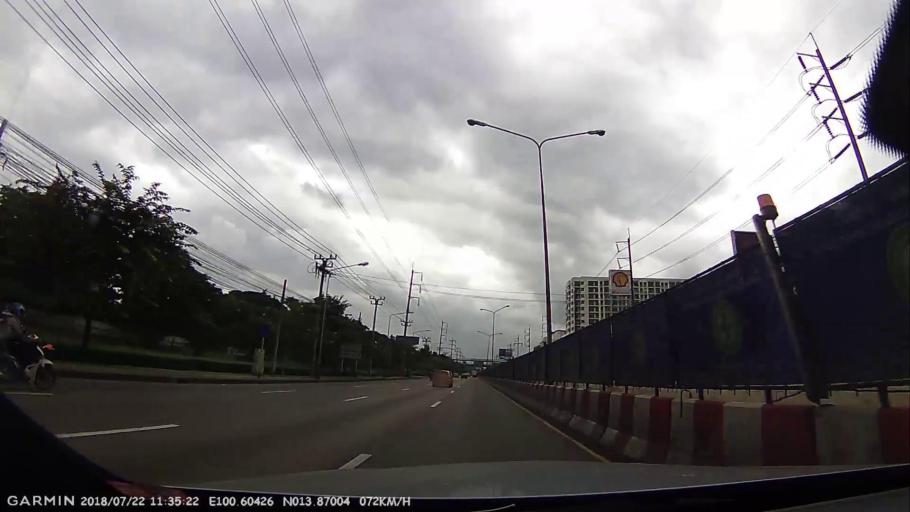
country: TH
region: Bangkok
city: Bang Khen
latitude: 13.8701
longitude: 100.6041
